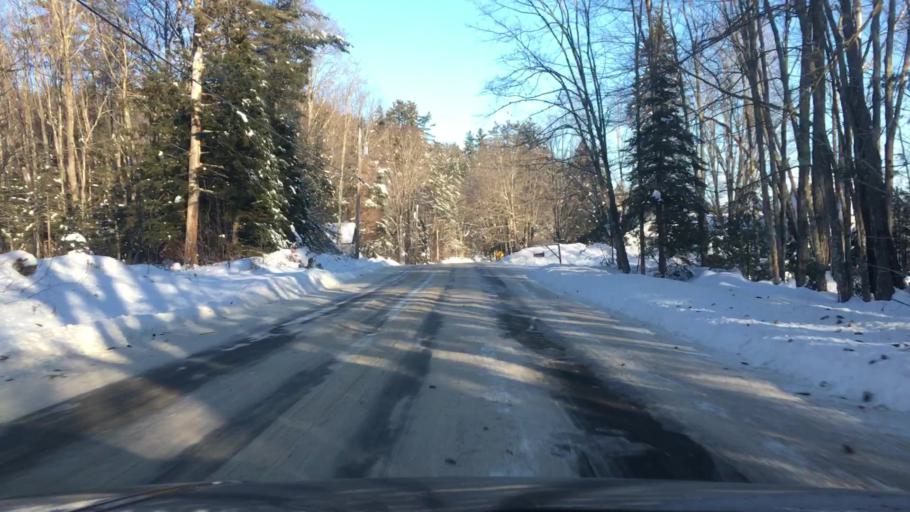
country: US
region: Maine
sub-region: Oxford County
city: Lovell
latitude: 44.1411
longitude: -70.9790
